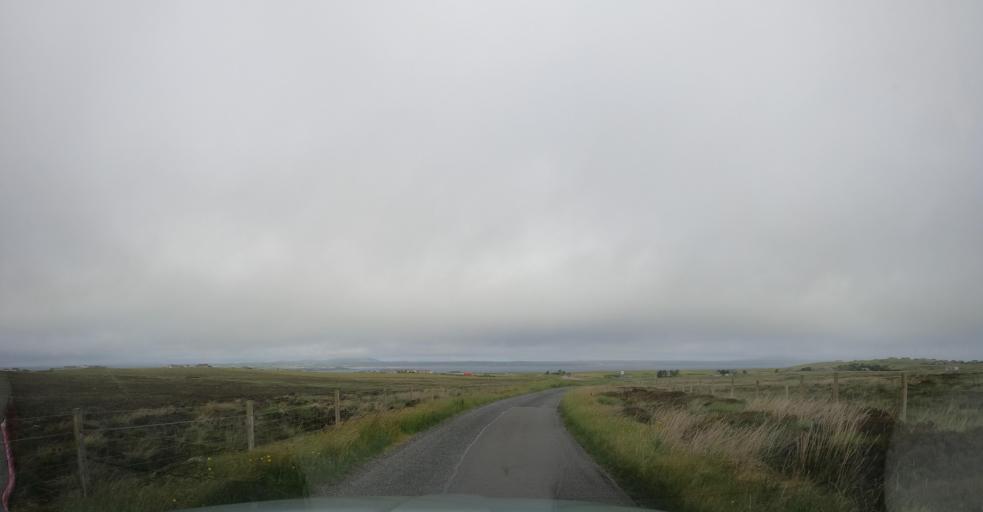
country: GB
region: Scotland
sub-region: Eilean Siar
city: Stornoway
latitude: 58.2048
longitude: -6.2460
